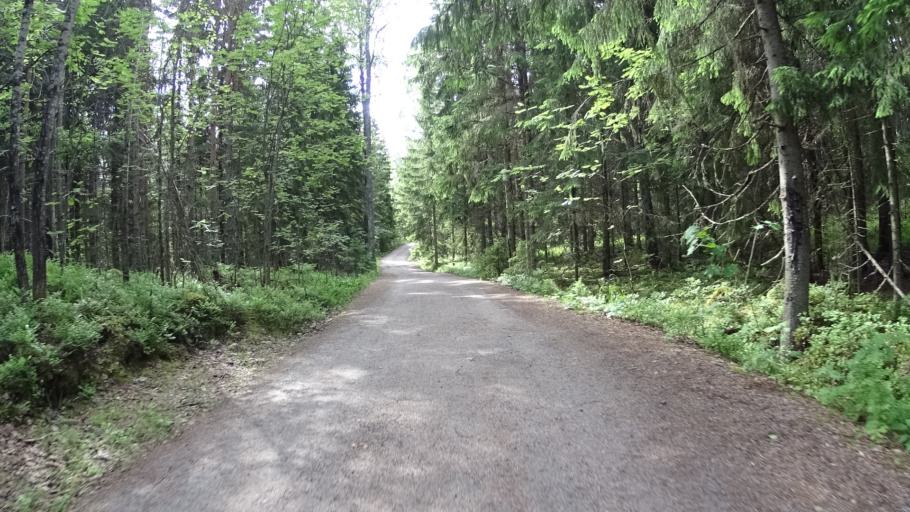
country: FI
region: Uusimaa
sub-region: Helsinki
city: Espoo
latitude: 60.2924
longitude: 24.5225
